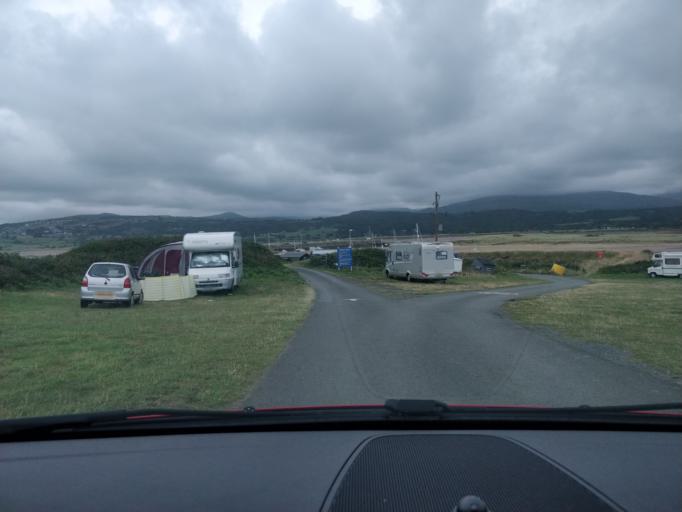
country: GB
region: Wales
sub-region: Gwynedd
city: Llanfair
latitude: 52.8237
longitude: -4.1362
